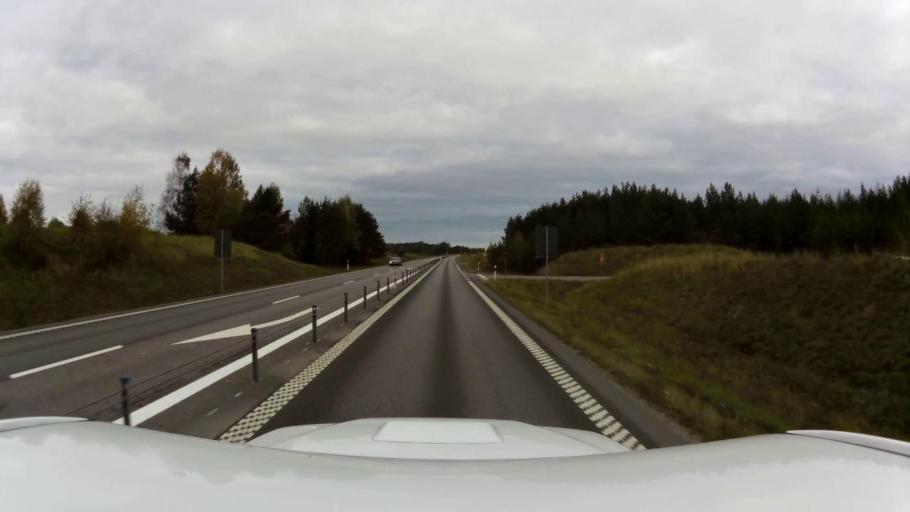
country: SE
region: OEstergoetland
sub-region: Linkopings Kommun
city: Ljungsbro
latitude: 58.4945
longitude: 15.4637
